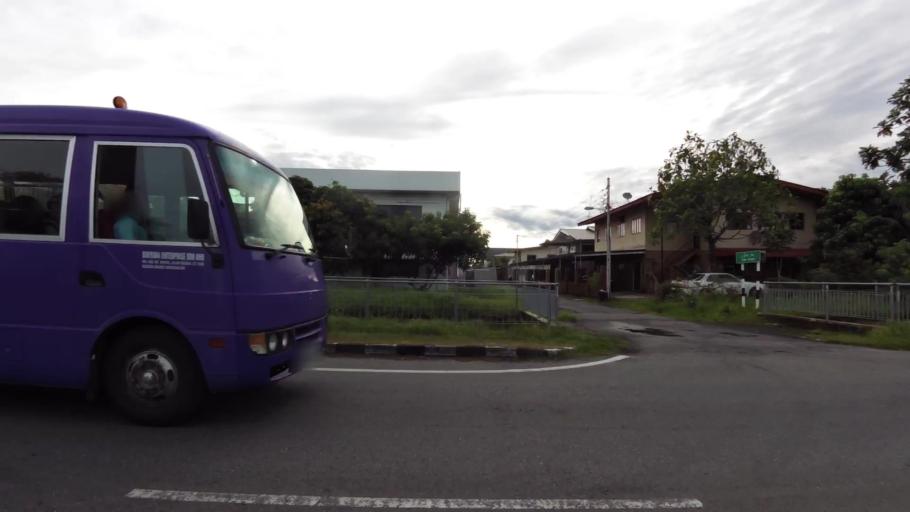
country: BN
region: Belait
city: Seria
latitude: 4.6102
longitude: 114.3275
